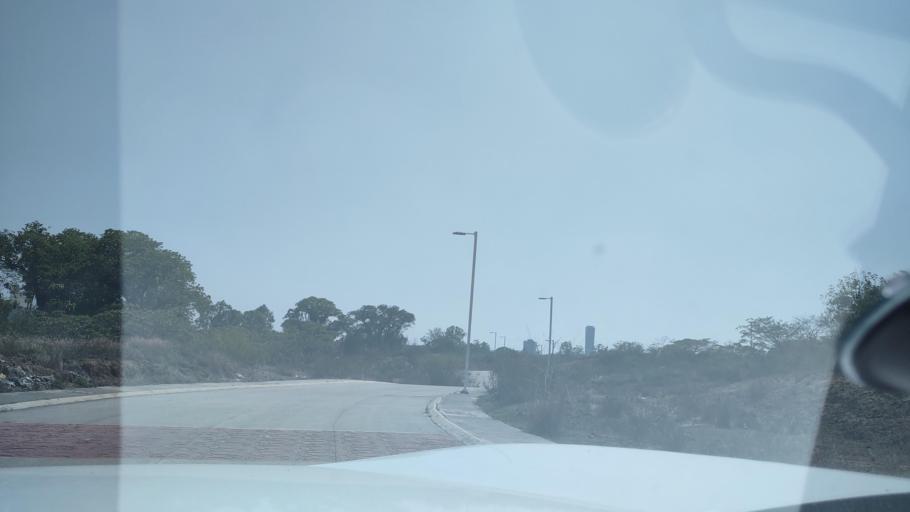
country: MX
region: Veracruz
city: El Castillo
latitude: 19.5279
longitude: -96.8674
